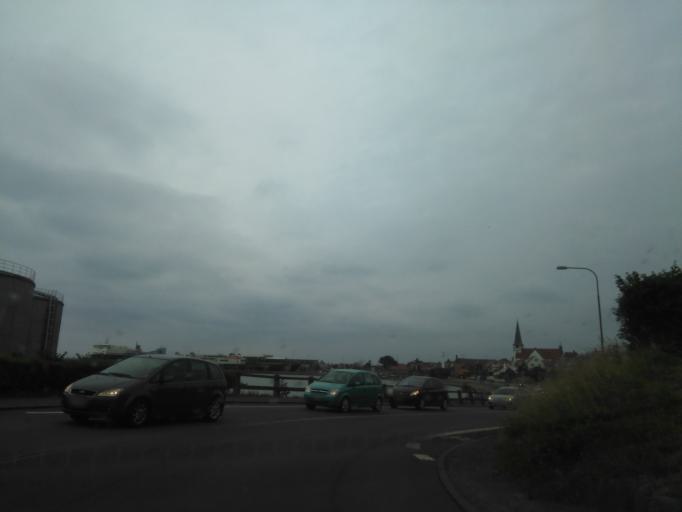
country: DK
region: Capital Region
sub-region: Bornholm Kommune
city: Ronne
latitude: 55.0948
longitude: 14.6992
